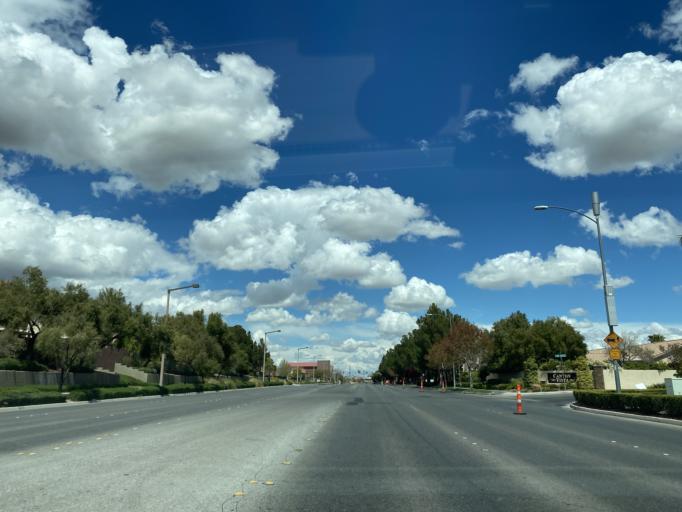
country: US
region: Nevada
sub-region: Clark County
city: Summerlin South
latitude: 36.1493
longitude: -115.3155
